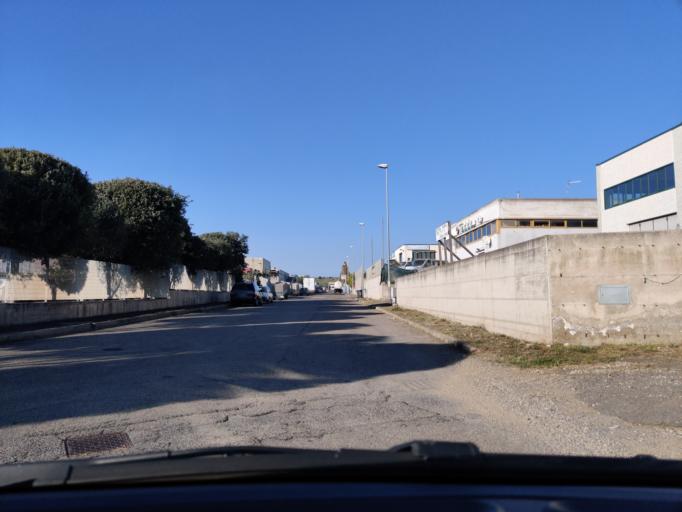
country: IT
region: Latium
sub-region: Citta metropolitana di Roma Capitale
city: Aurelia
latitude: 42.1176
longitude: 11.7809
